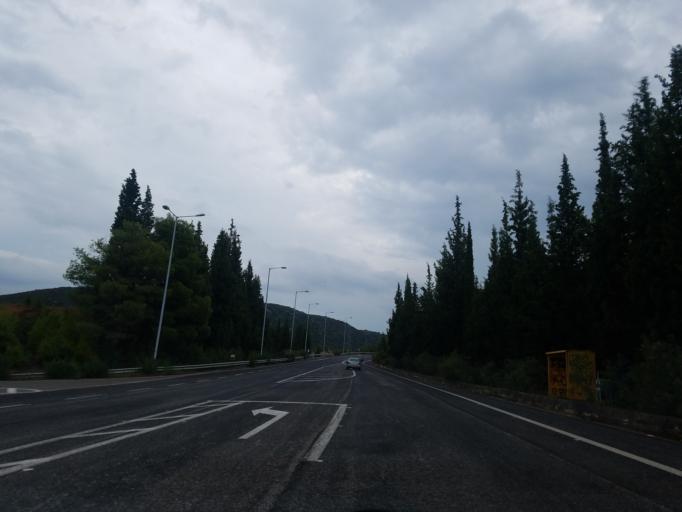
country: GR
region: Central Greece
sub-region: Nomos Voiotias
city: Livadeia
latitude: 38.4472
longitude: 22.7934
